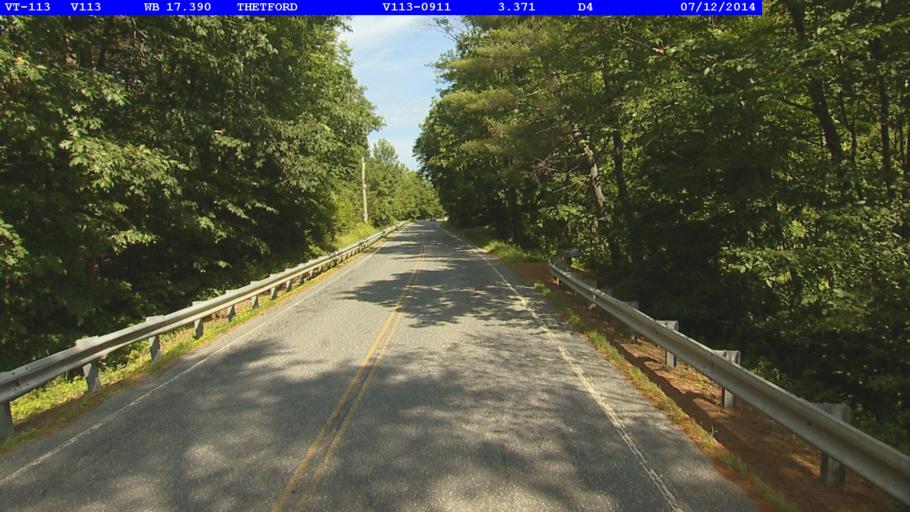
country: US
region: New Hampshire
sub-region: Grafton County
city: Lyme
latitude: 43.8509
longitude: -72.2566
